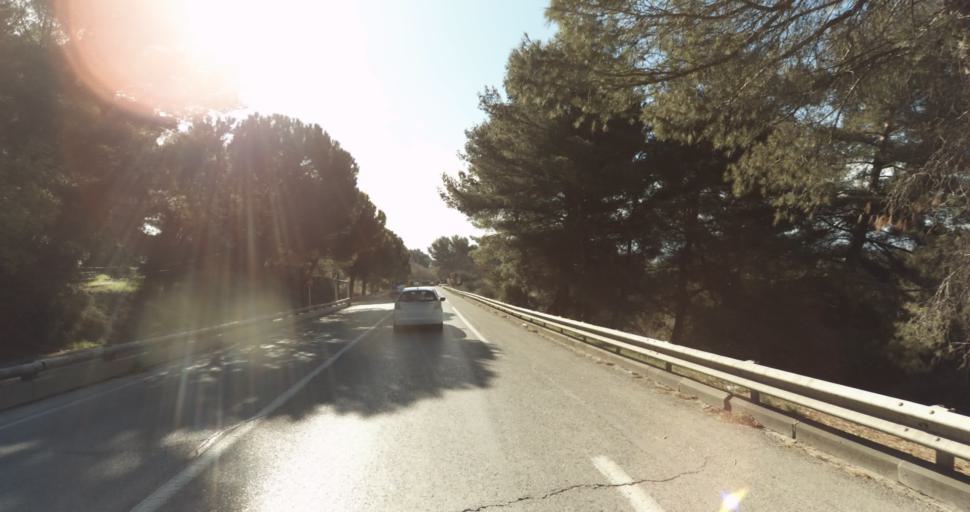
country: FR
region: Provence-Alpes-Cote d'Azur
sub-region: Departement des Bouches-du-Rhone
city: Aix-en-Provence
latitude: 43.5513
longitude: 5.4375
